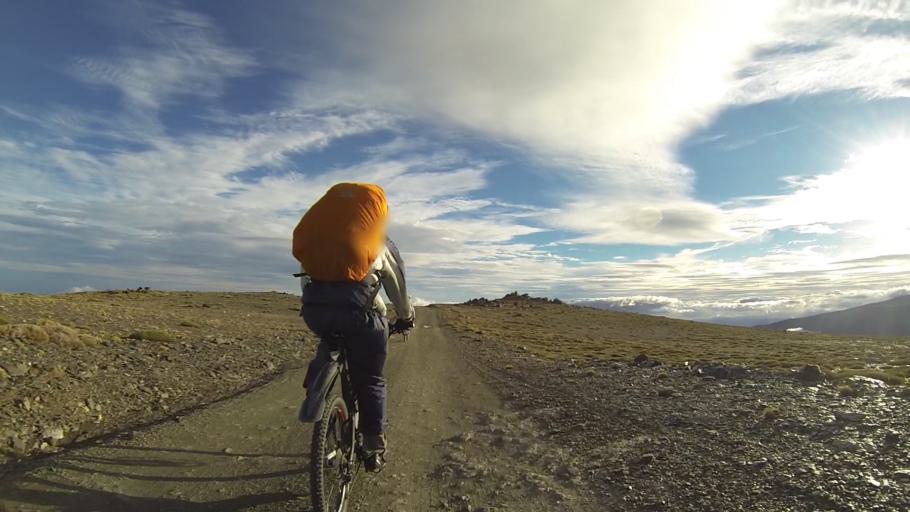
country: ES
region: Andalusia
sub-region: Provincia de Granada
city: Trevelez
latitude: 37.0044
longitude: -3.3078
